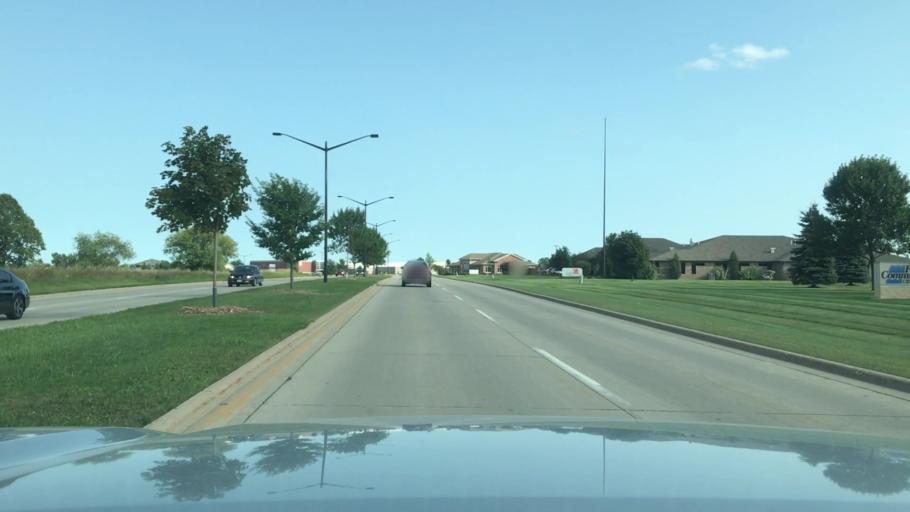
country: US
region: Wisconsin
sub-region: Brown County
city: Bellevue
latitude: 44.4866
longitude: -87.9249
